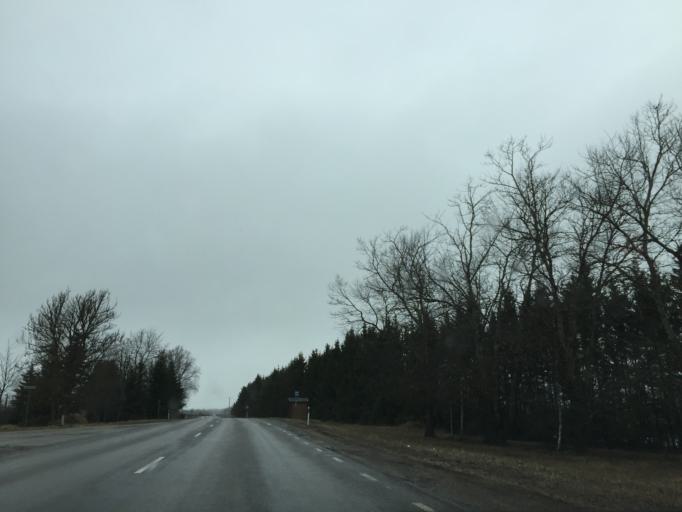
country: EE
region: Laeaene
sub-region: Ridala Parish
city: Uuemoisa
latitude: 58.8787
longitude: 23.6074
